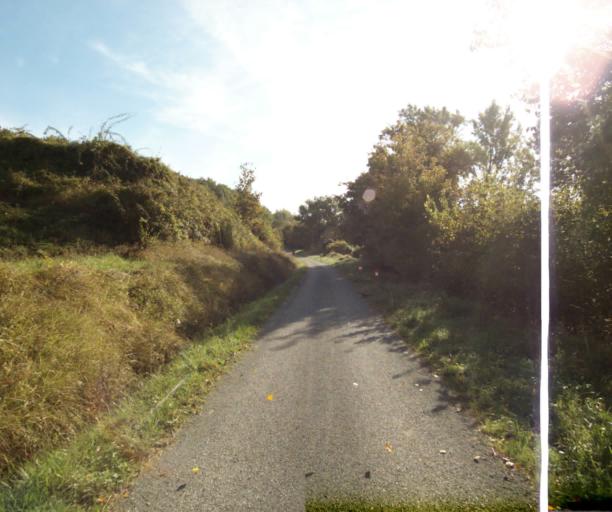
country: FR
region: Midi-Pyrenees
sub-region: Departement du Tarn-et-Garonne
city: Nohic
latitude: 43.9004
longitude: 1.4638
